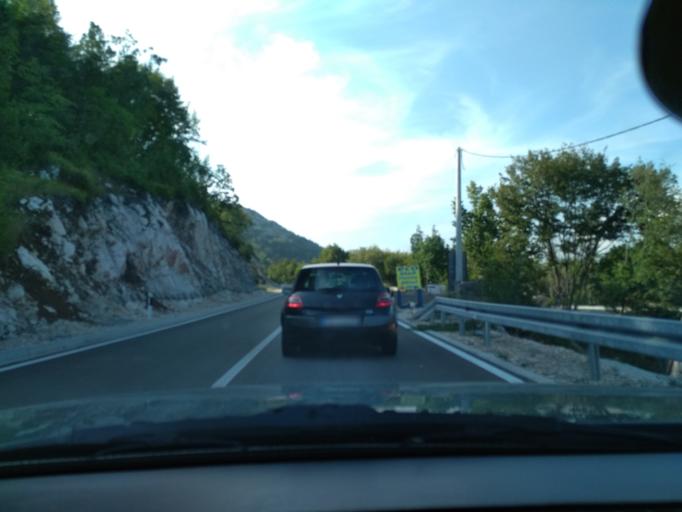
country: ME
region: Cetinje
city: Cetinje
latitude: 42.4164
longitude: 18.8795
